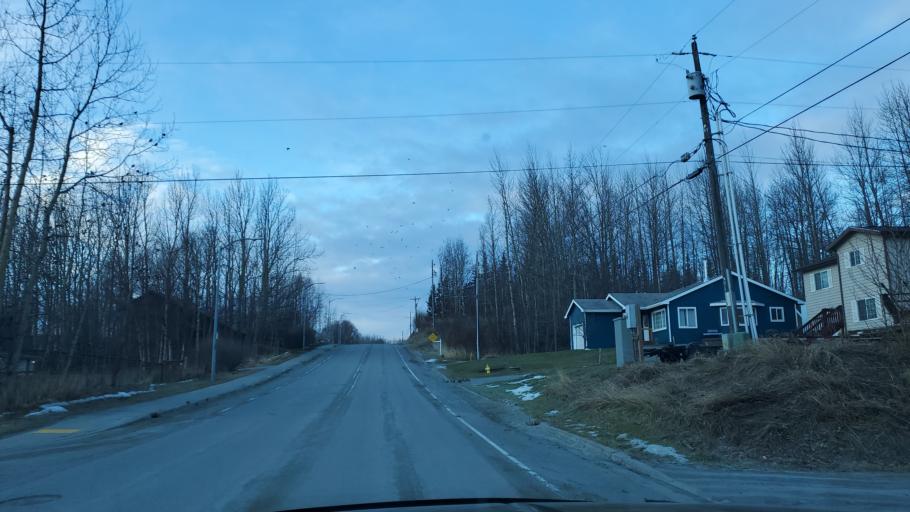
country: US
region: Alaska
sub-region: Matanuska-Susitna Borough
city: Palmer
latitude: 61.6139
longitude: -149.1107
